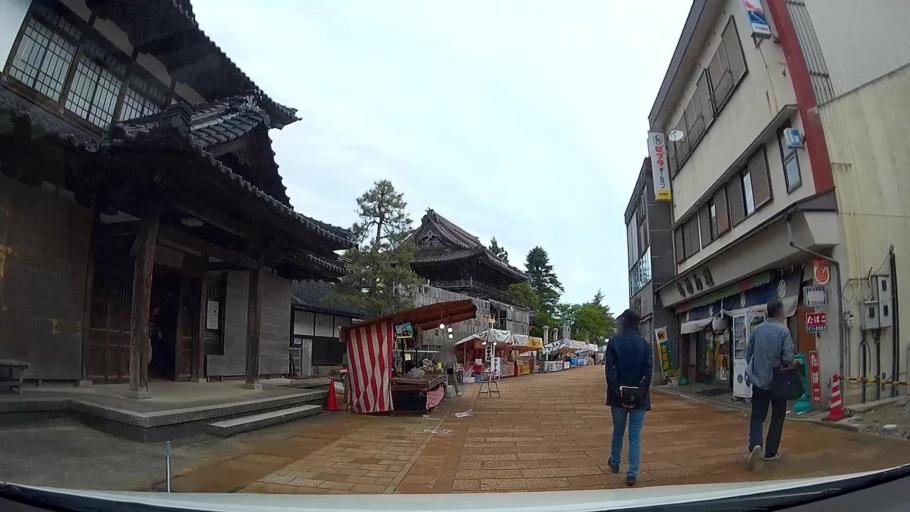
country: JP
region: Toyama
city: Fukumitsu
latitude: 36.5150
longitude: 136.9016
